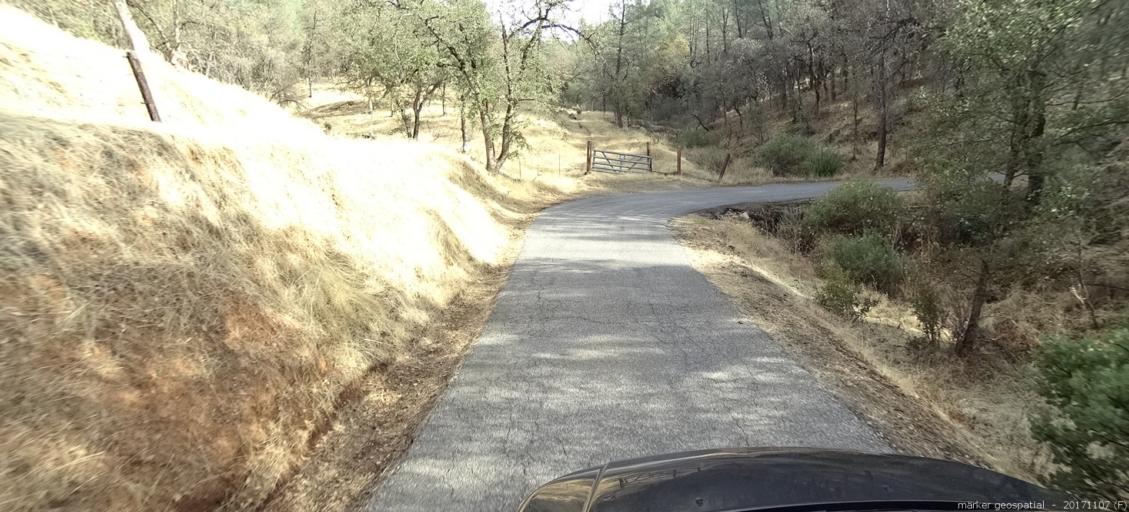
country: US
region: California
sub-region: Shasta County
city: Shasta
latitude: 40.5326
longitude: -122.5256
